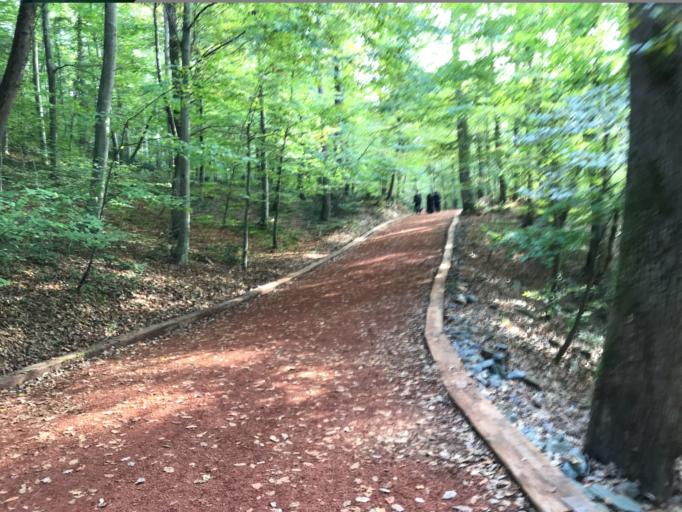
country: TR
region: Istanbul
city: Kemerburgaz
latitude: 41.1789
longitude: 28.9598
